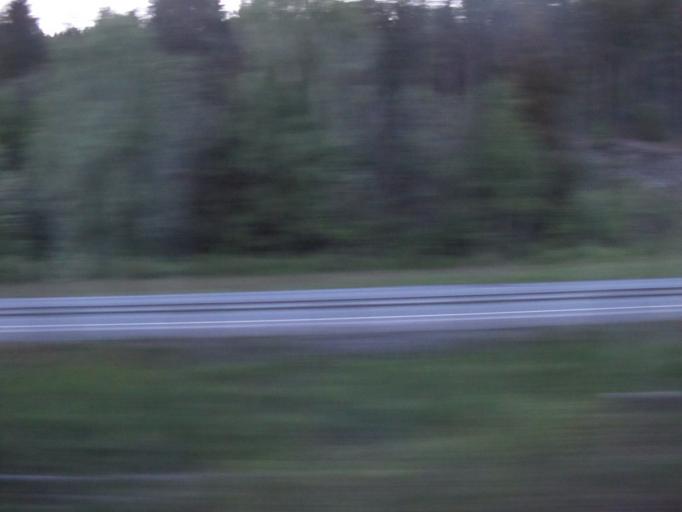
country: NO
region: Oppland
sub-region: Ringebu
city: Ringebu
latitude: 61.5395
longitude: 10.0898
